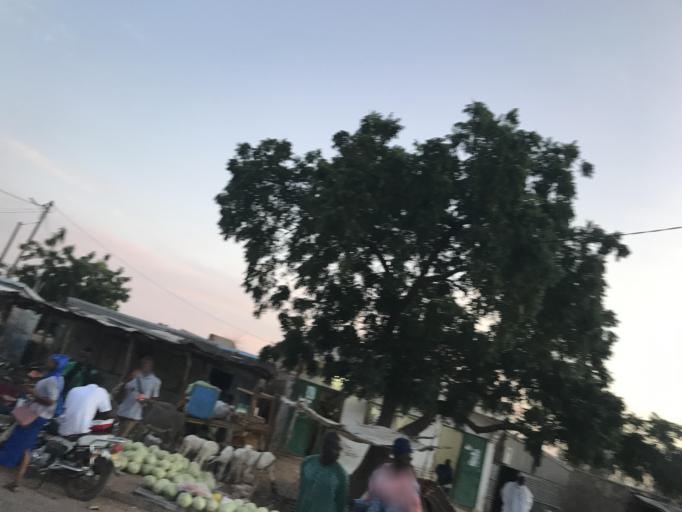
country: SN
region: Matam
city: Ranerou
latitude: 15.2982
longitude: -13.9609
